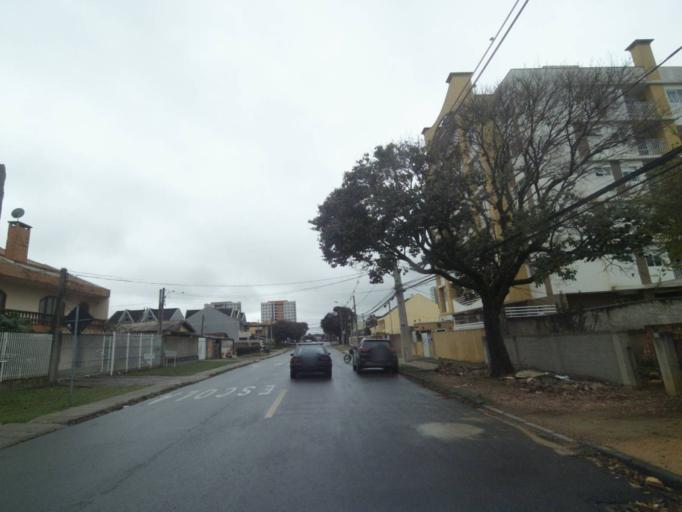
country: BR
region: Parana
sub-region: Curitiba
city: Curitiba
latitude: -25.5016
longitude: -49.3007
